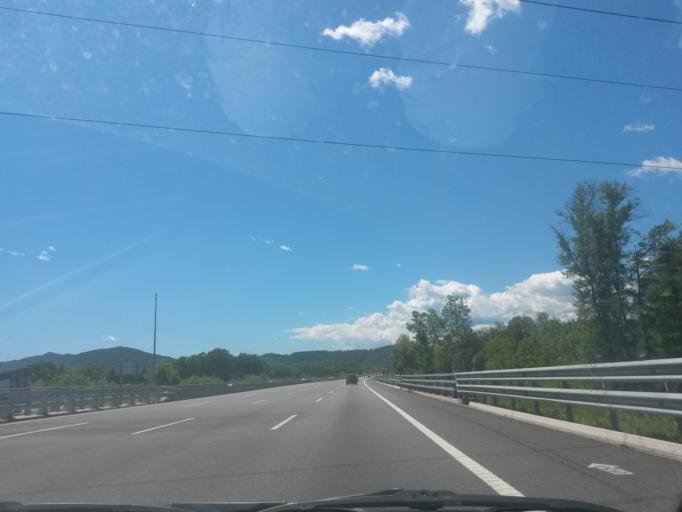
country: ES
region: Catalonia
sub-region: Provincia de Girona
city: Celra
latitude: 42.0530
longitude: 2.8778
